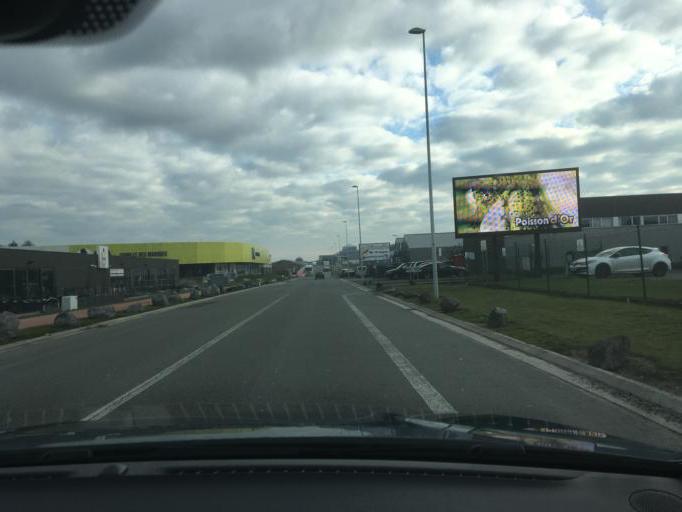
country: BE
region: Wallonia
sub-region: Province du Hainaut
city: Estaimpuis
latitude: 50.7170
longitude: 3.2763
